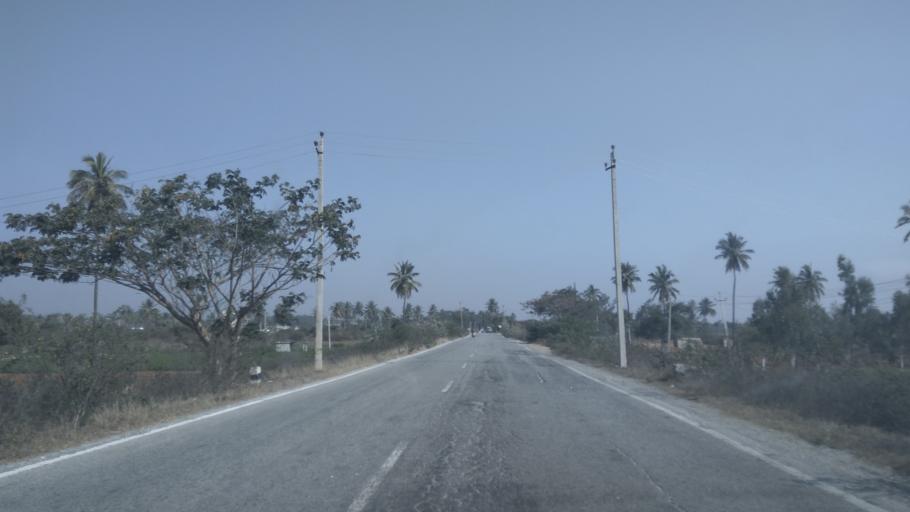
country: IN
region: Karnataka
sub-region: Bangalore Rural
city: Devanhalli
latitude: 13.2086
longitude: 77.7411
